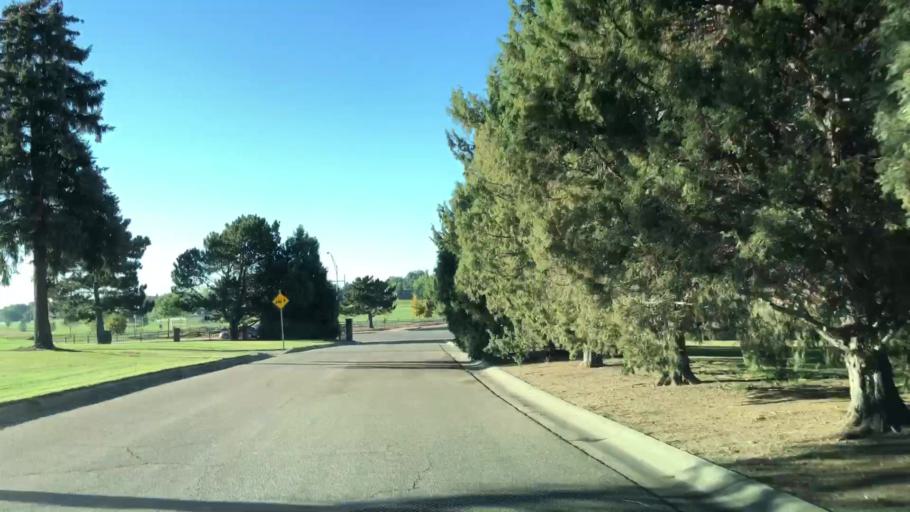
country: US
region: Colorado
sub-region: Larimer County
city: Loveland
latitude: 40.4226
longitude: -105.1051
